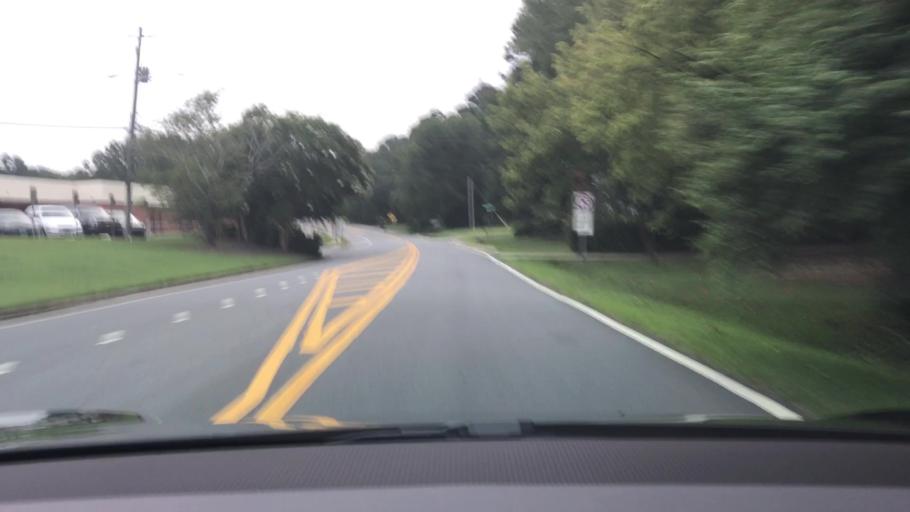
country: US
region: Georgia
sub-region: Gwinnett County
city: Suwanee
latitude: 34.0848
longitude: -84.0704
